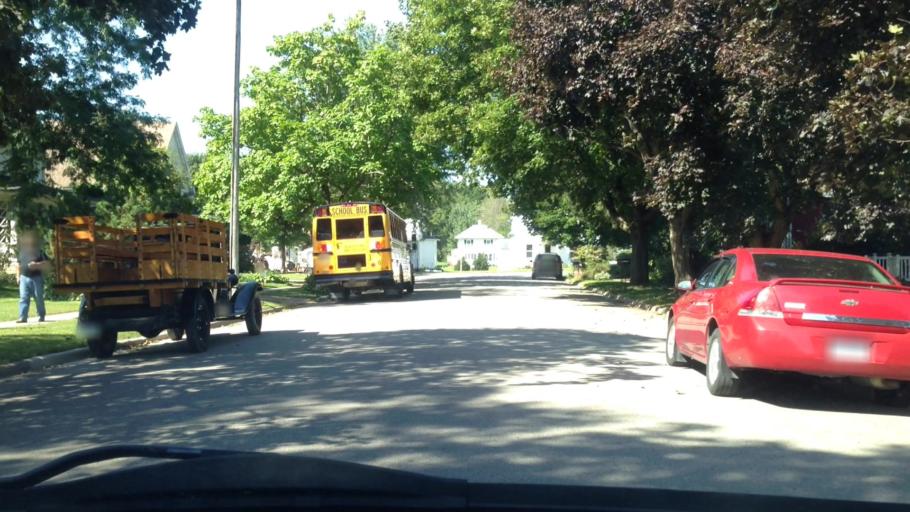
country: US
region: Minnesota
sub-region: Houston County
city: Spring Grove
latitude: 43.5215
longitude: -91.7734
